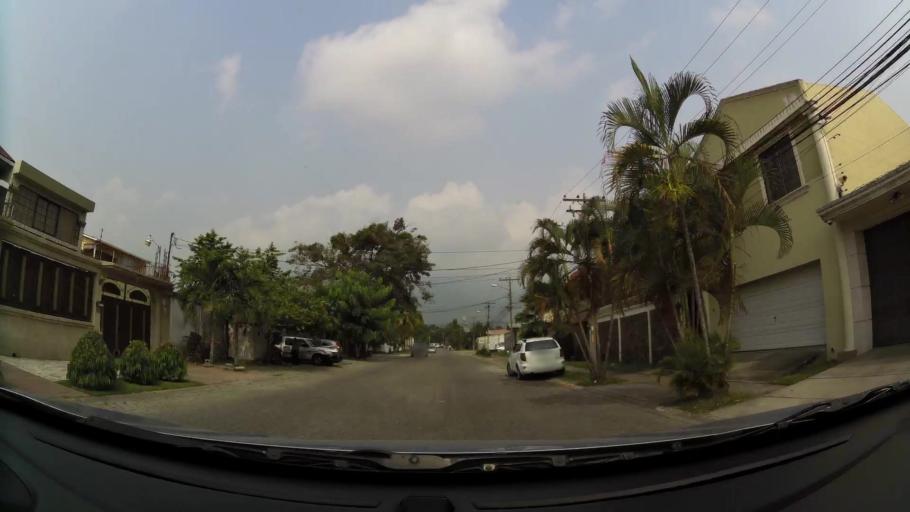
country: HN
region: Cortes
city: San Pedro Sula
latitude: 15.5244
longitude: -88.0288
